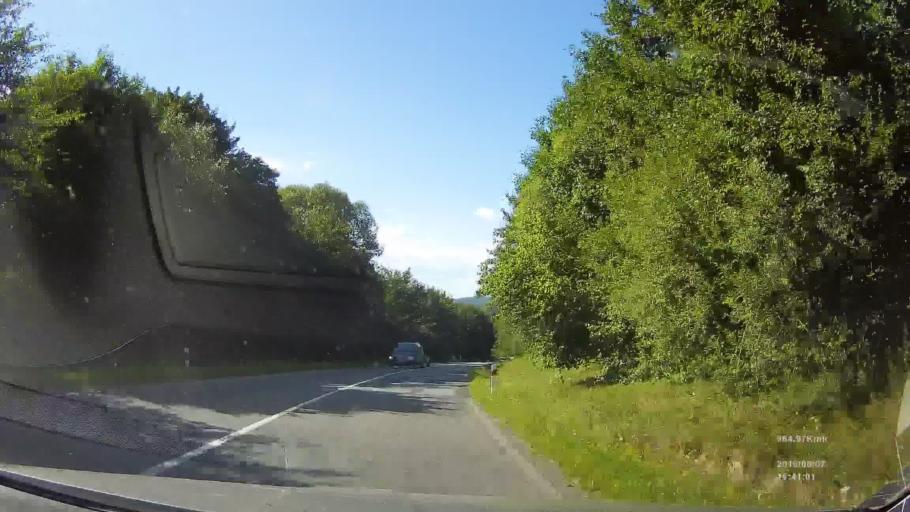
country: SK
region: Presovsky
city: Giraltovce
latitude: 49.1219
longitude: 21.5832
